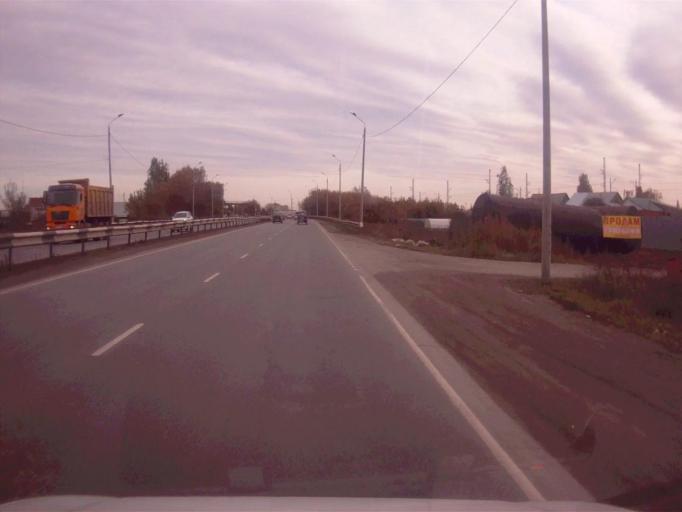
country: RU
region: Chelyabinsk
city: Novosineglazovskiy
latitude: 55.0443
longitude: 61.4226
